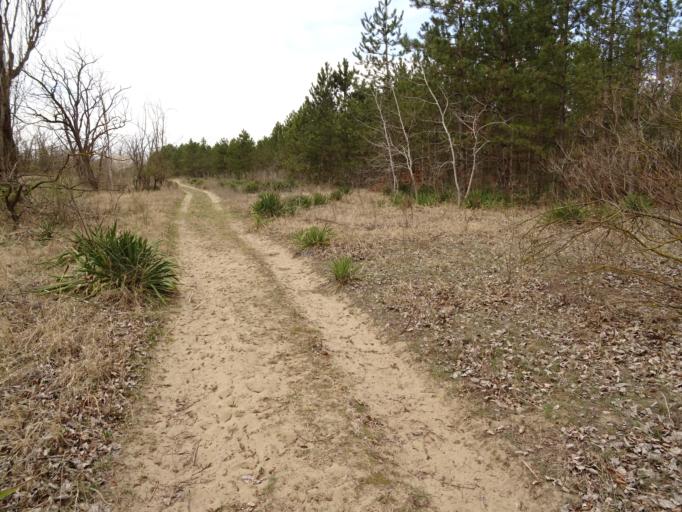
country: HU
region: Bacs-Kiskun
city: Izsak
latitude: 46.7706
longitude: 19.3323
